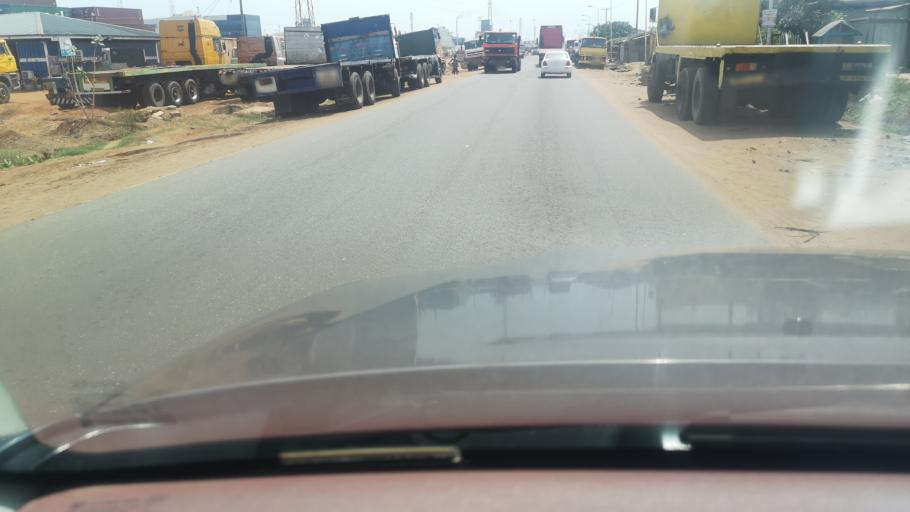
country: GH
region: Greater Accra
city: Tema
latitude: 5.6294
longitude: -0.0086
